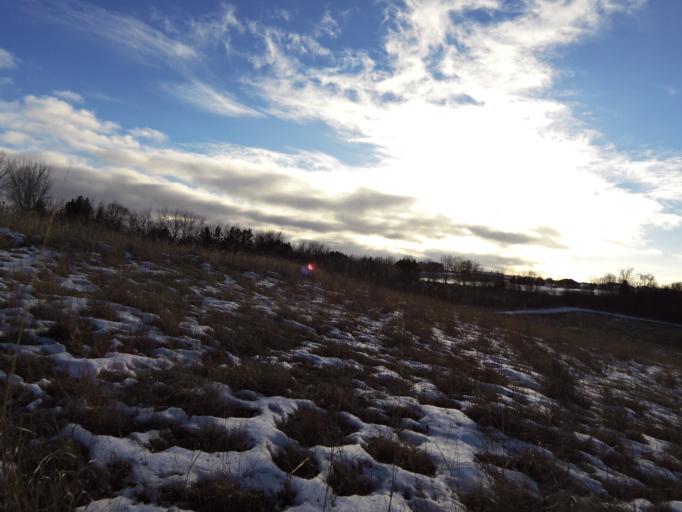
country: US
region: Wisconsin
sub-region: Pierce County
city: Prescott
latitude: 44.7983
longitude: -92.8246
